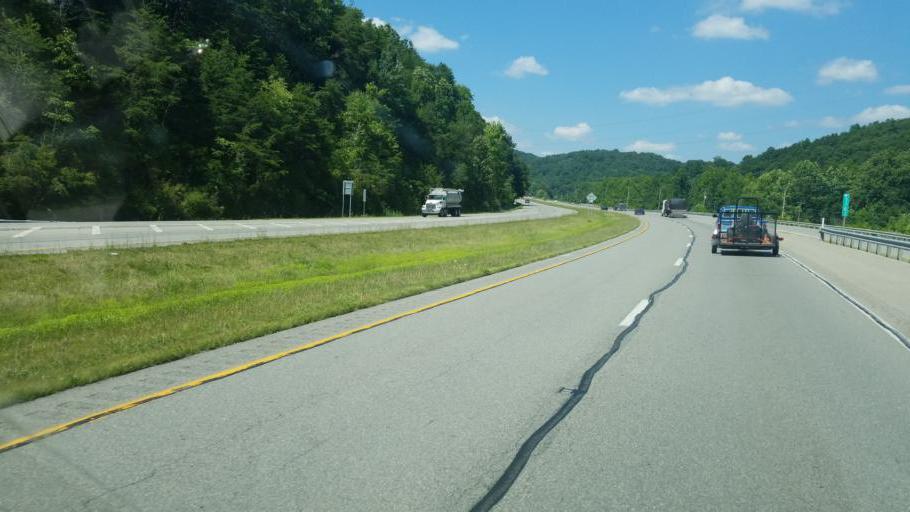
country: US
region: West Virginia
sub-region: Kanawha County
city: Sissonville
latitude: 38.5462
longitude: -81.6358
